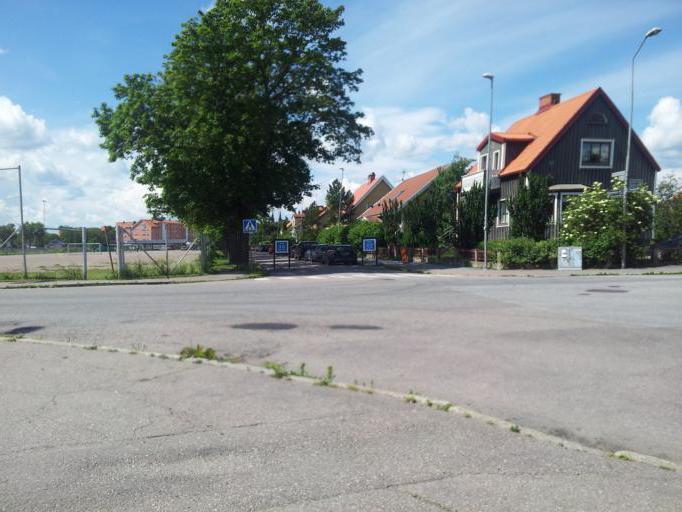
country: SE
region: Uppsala
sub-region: Uppsala Kommun
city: Uppsala
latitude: 59.8581
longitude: 17.6654
